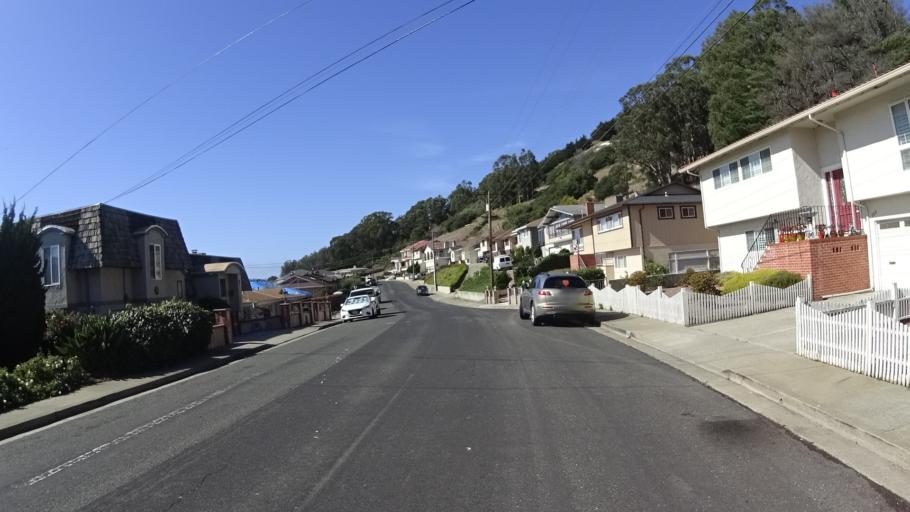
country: US
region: California
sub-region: San Mateo County
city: South San Francisco
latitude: 37.6616
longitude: -122.4165
